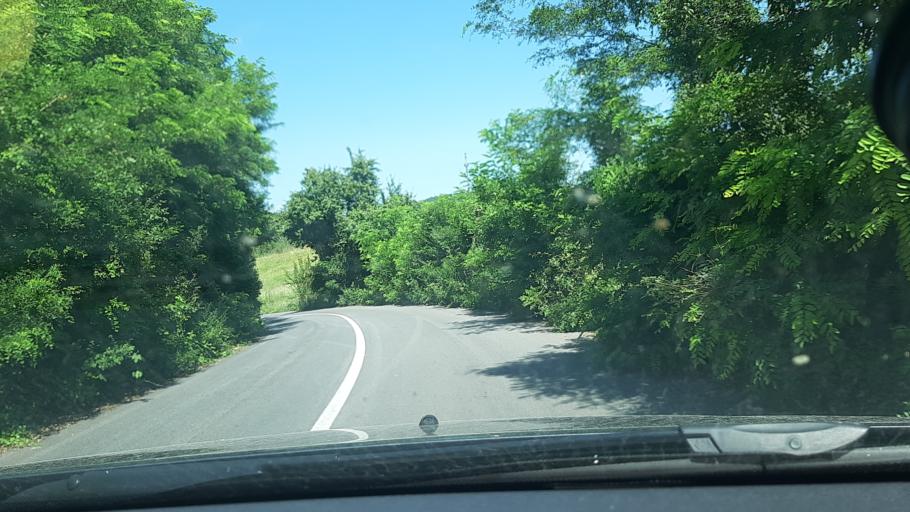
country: RO
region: Hunedoara
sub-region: Comuna Teliucu Inferior
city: Teliucu Inferior
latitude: 45.6972
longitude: 22.8792
